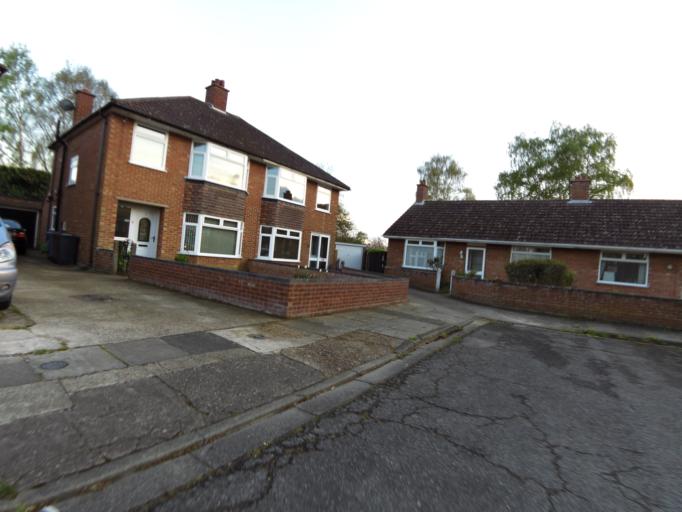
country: GB
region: England
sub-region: Suffolk
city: Kesgrave
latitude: 52.0684
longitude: 1.1989
